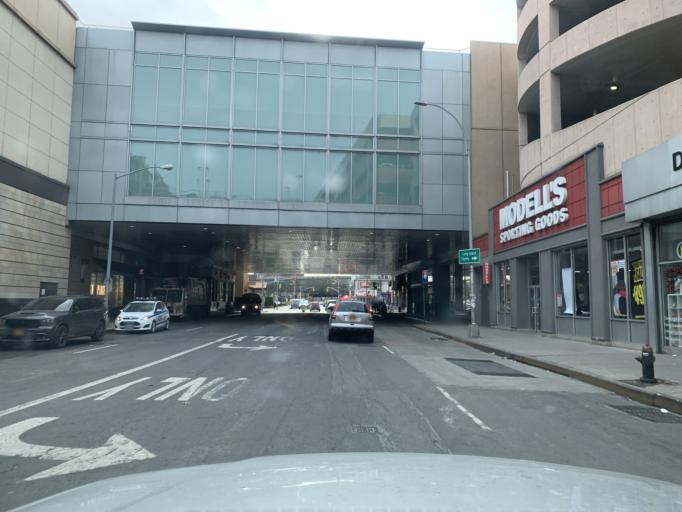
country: US
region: New York
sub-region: Queens County
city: Borough of Queens
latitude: 40.7351
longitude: -73.8696
